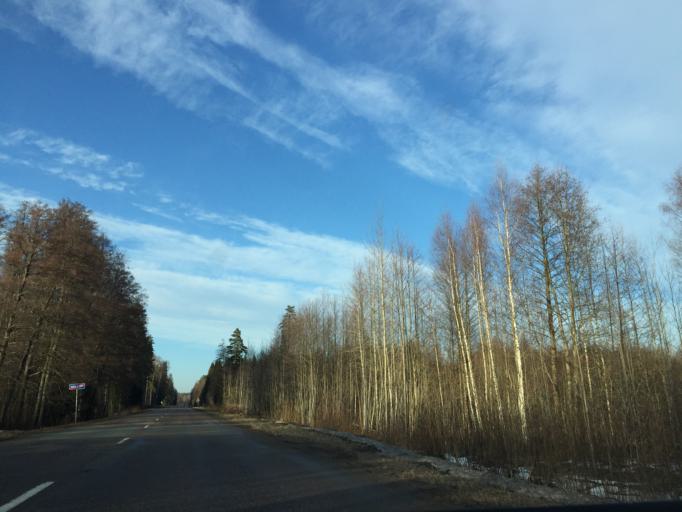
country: LV
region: Kekava
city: Balozi
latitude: 56.7385
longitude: 24.1088
